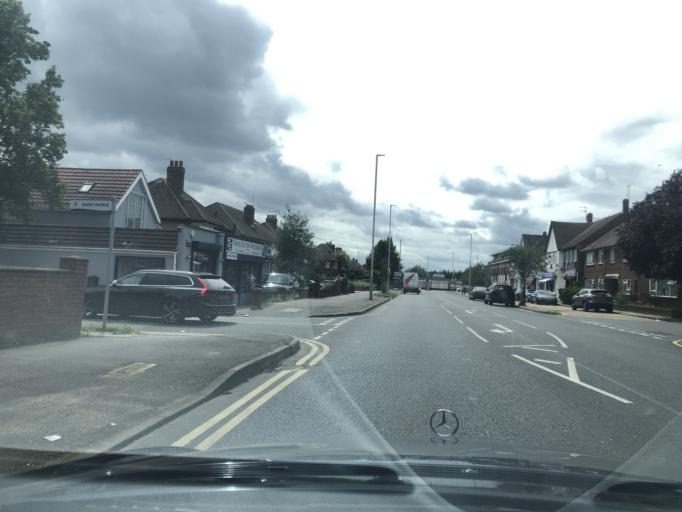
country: GB
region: England
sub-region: Greater London
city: Ruislip
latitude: 51.5548
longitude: -0.4020
